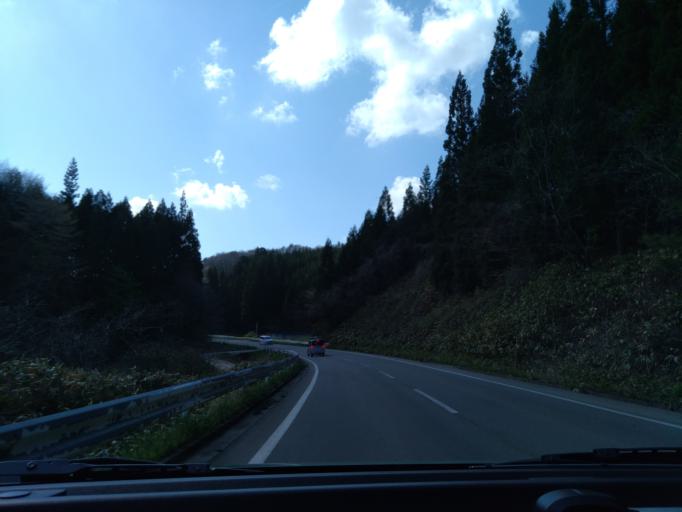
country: JP
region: Akita
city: Akita
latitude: 39.6954
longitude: 140.2378
